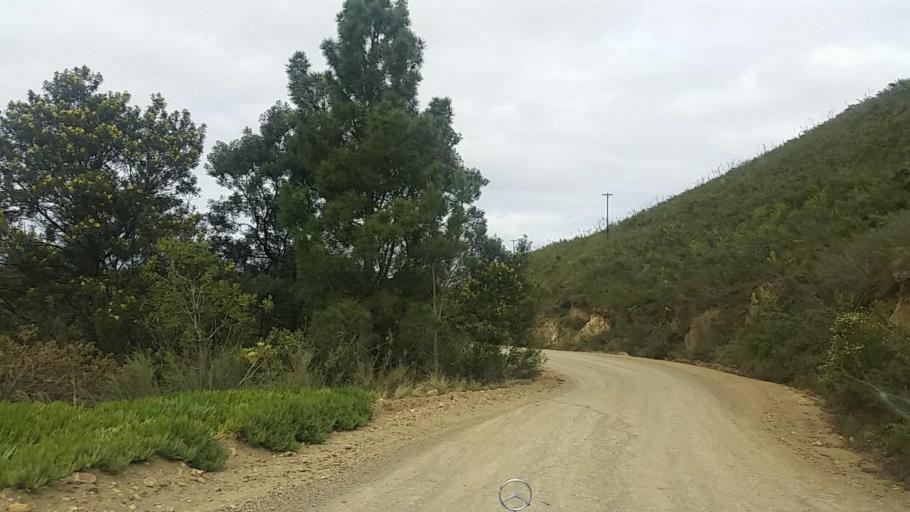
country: ZA
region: Western Cape
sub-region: Eden District Municipality
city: Knysna
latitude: -33.7584
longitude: 23.1557
